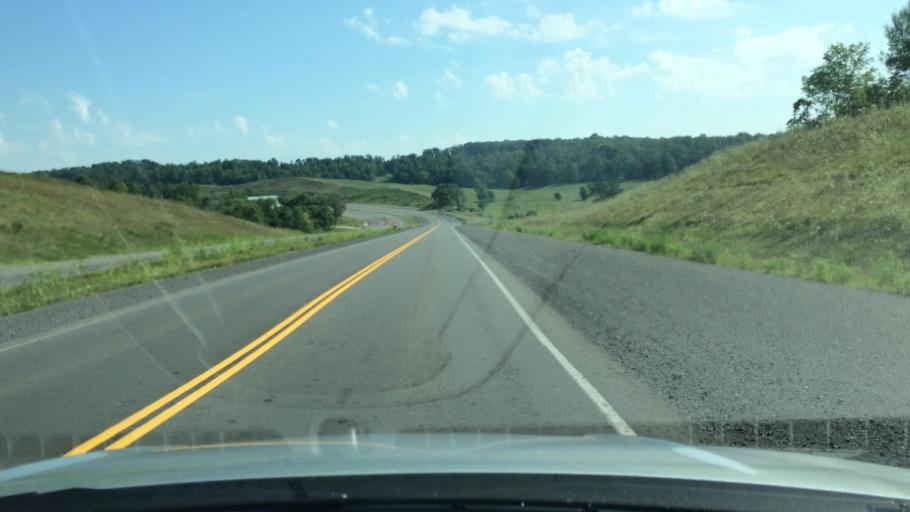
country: US
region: Tennessee
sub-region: Jefferson County
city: White Pine
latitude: 36.1204
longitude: -83.3371
